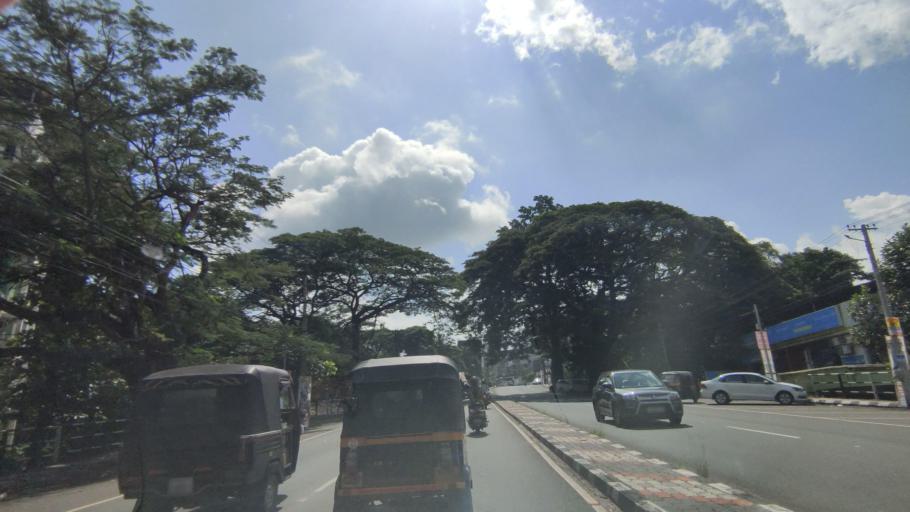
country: IN
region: Kerala
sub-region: Kottayam
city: Kottayam
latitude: 9.5919
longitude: 76.5296
